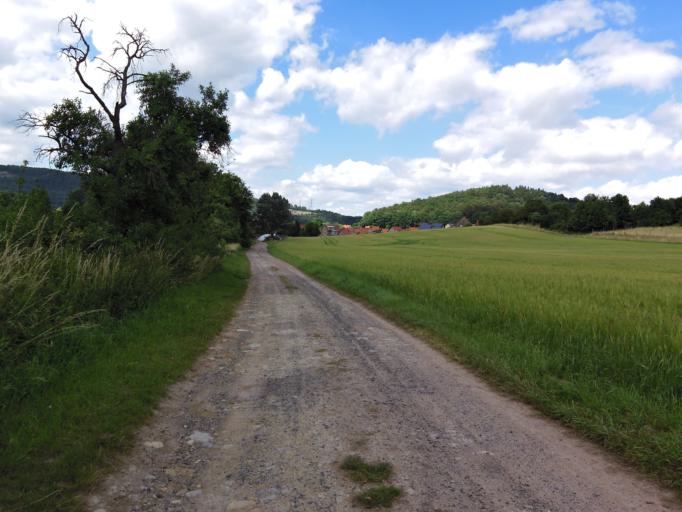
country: DE
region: Hesse
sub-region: Regierungsbezirk Kassel
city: Herleshausen
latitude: 50.9945
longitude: 10.2153
